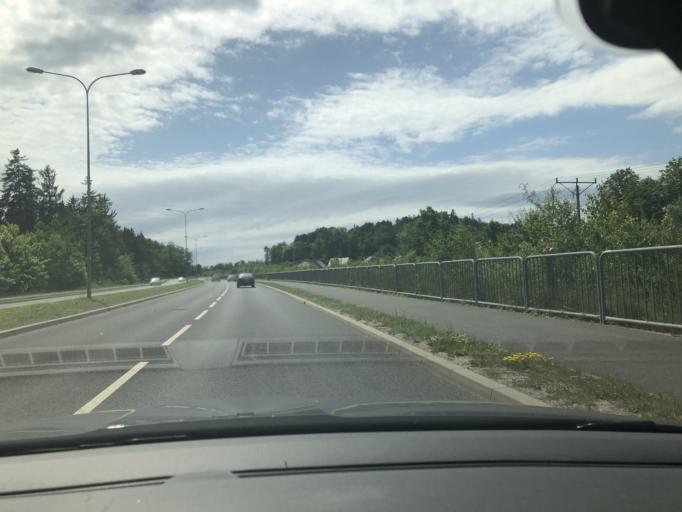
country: PL
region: Lower Silesian Voivodeship
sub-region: Jelenia Gora
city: Jelenia Gora
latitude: 50.8957
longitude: 15.7682
